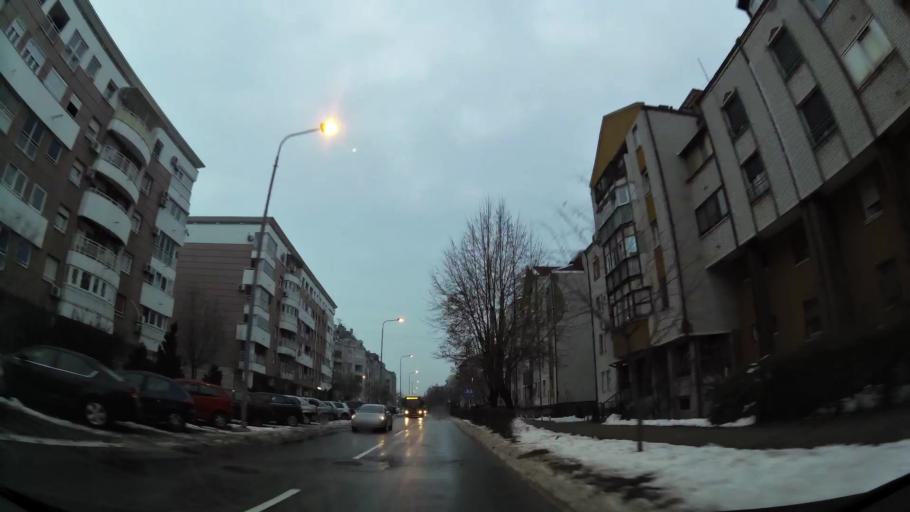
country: RS
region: Central Serbia
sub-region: Belgrade
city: Zemun
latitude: 44.8129
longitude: 20.3717
